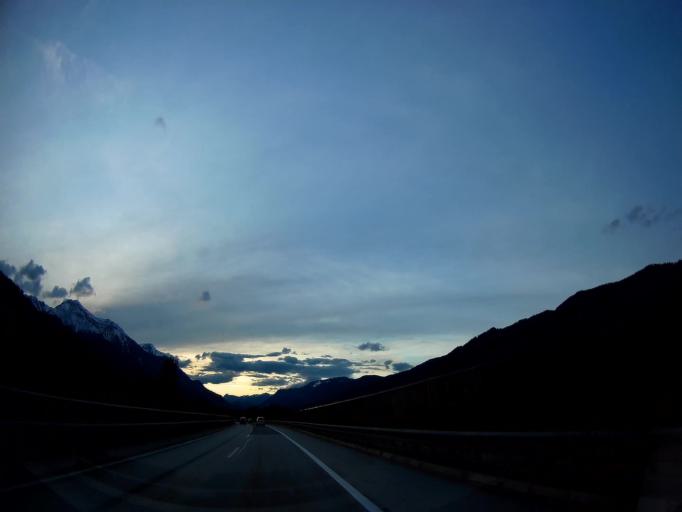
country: AT
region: Styria
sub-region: Politischer Bezirk Liezen
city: Selzthal
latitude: 47.5517
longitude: 14.3585
